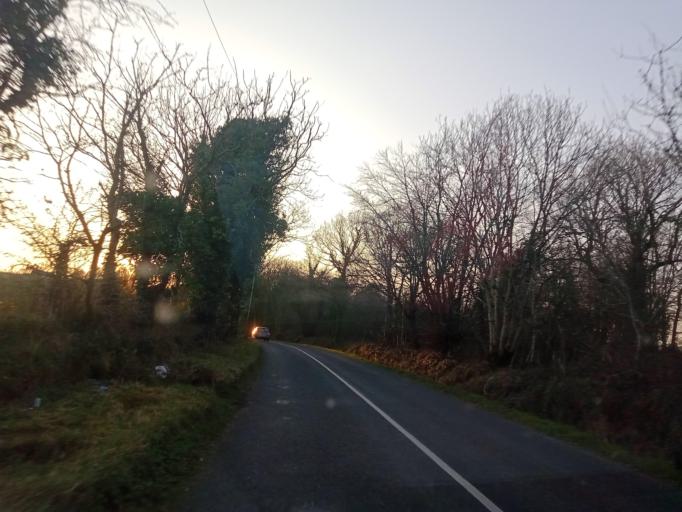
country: IE
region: Leinster
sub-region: Kilkenny
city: Castlecomer
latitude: 52.8403
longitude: -7.2540
